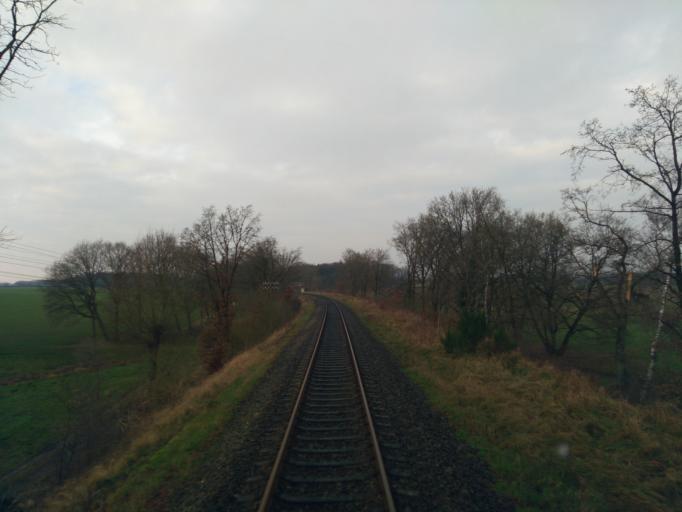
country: DE
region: Lower Saxony
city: Kirchlinteln
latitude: 52.9608
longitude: 9.2731
